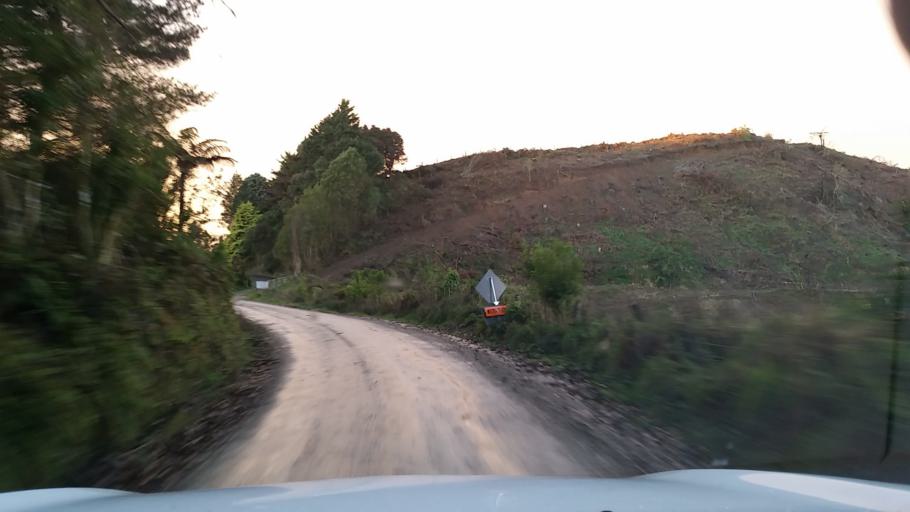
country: NZ
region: Manawatu-Wanganui
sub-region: Wanganui District
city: Wanganui
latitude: -39.7710
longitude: 174.8714
